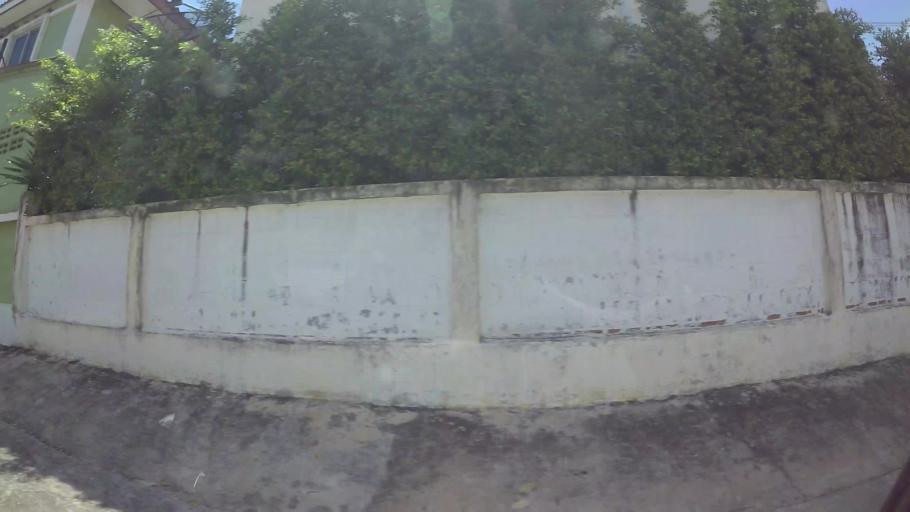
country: TH
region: Chon Buri
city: Ban Talat Bueng
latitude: 13.1139
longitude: 100.9566
